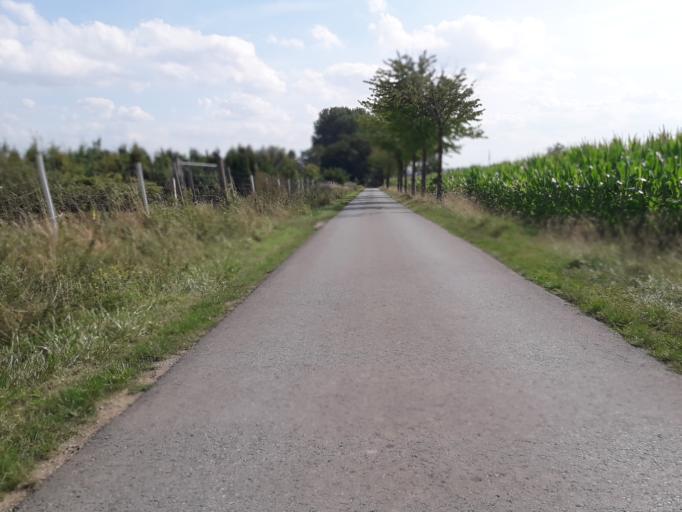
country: DE
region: North Rhine-Westphalia
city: Bad Lippspringe
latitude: 51.7563
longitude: 8.7951
